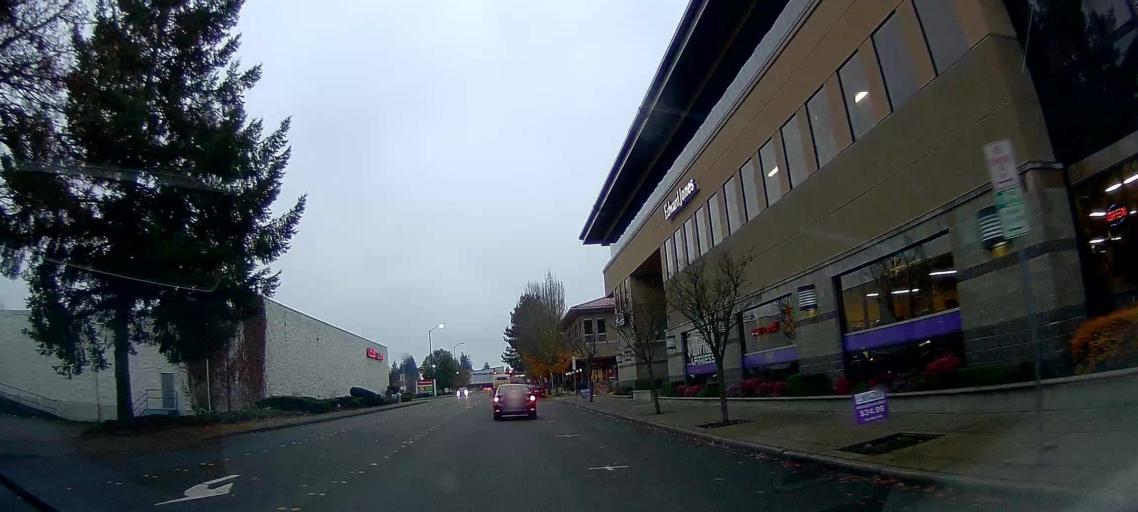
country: US
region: Washington
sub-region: Thurston County
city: Lacey
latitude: 47.0433
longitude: -122.8309
